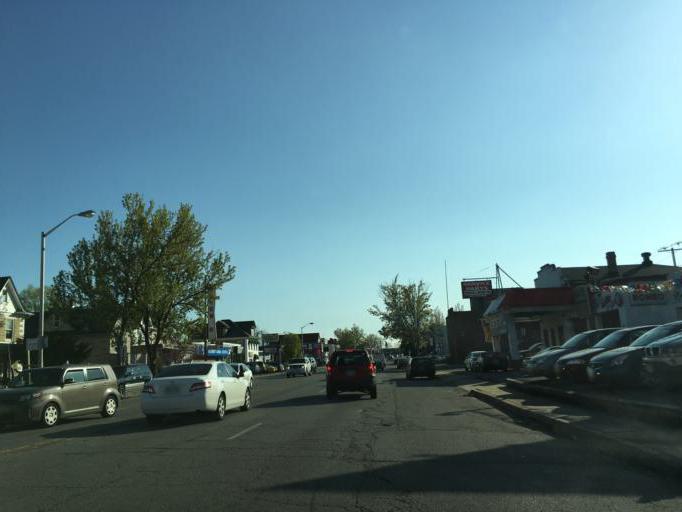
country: US
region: Maryland
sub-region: Baltimore County
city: Overlea
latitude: 39.3464
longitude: -76.5403
